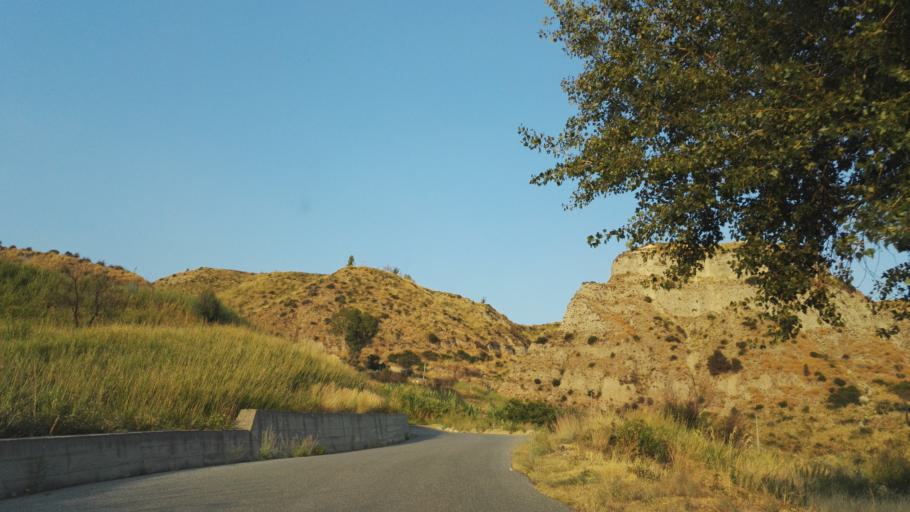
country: IT
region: Calabria
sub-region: Provincia di Reggio Calabria
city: Caulonia
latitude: 38.3957
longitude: 16.4293
